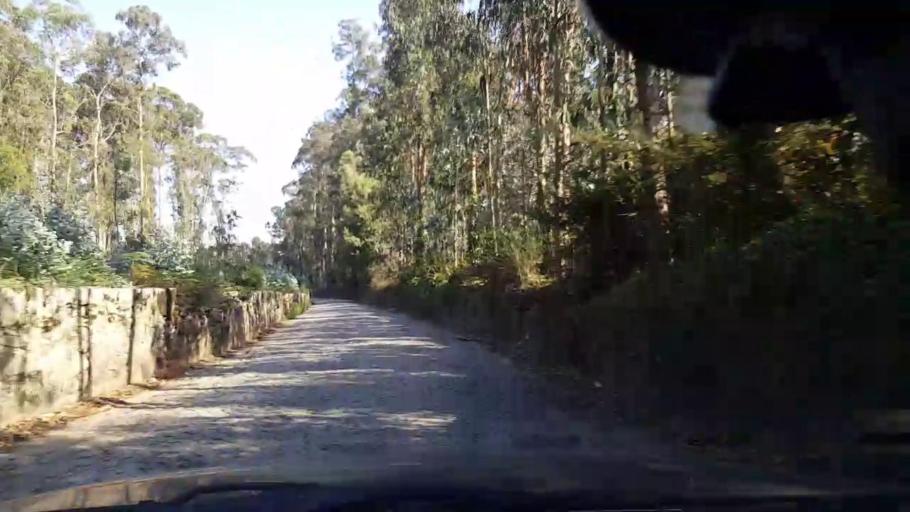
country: PT
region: Porto
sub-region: Vila do Conde
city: Arvore
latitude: 41.3513
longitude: -8.7017
